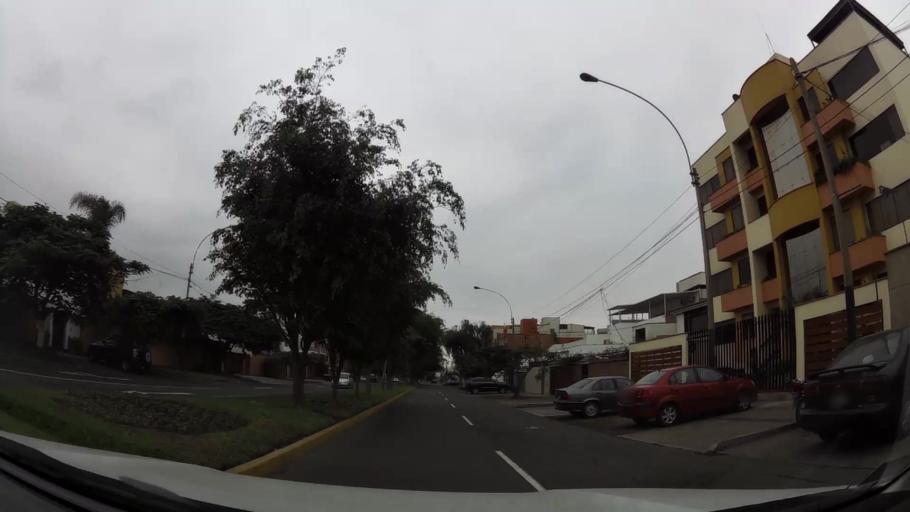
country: PE
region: Lima
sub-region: Lima
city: La Molina
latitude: -12.1111
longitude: -76.9737
